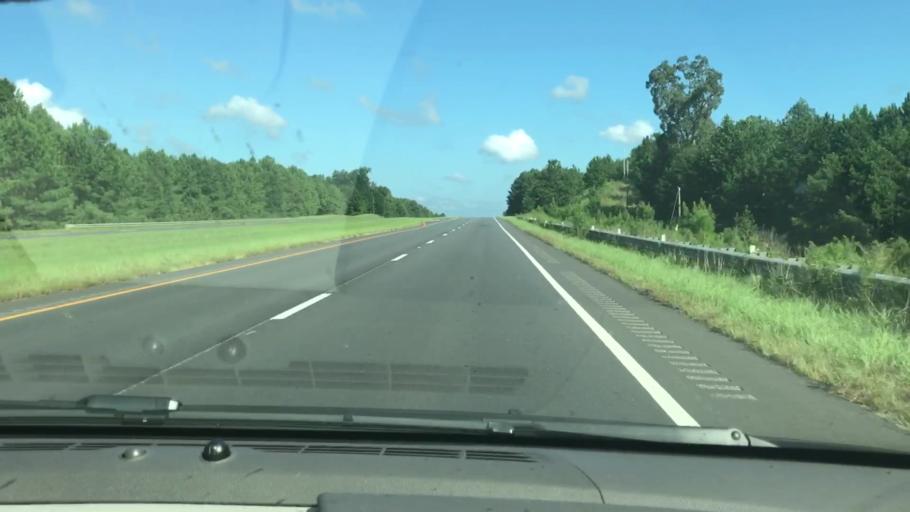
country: US
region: Alabama
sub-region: Barbour County
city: Eufaula
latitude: 32.0443
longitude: -85.1297
